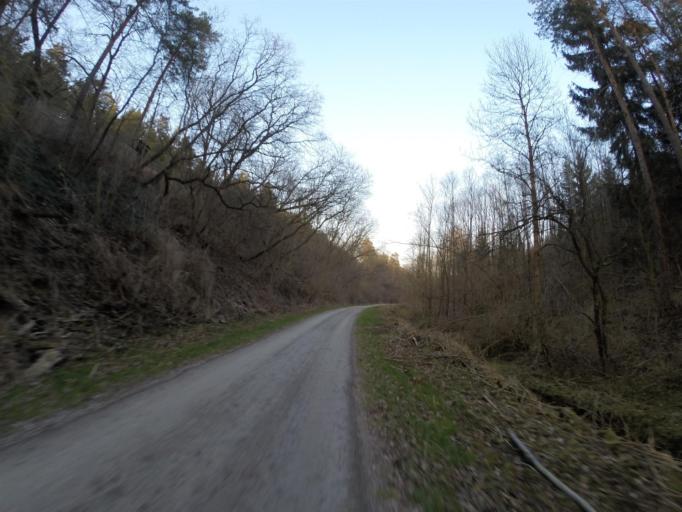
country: DE
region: Thuringia
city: Grossschwabhausen
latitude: 50.9452
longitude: 11.5161
